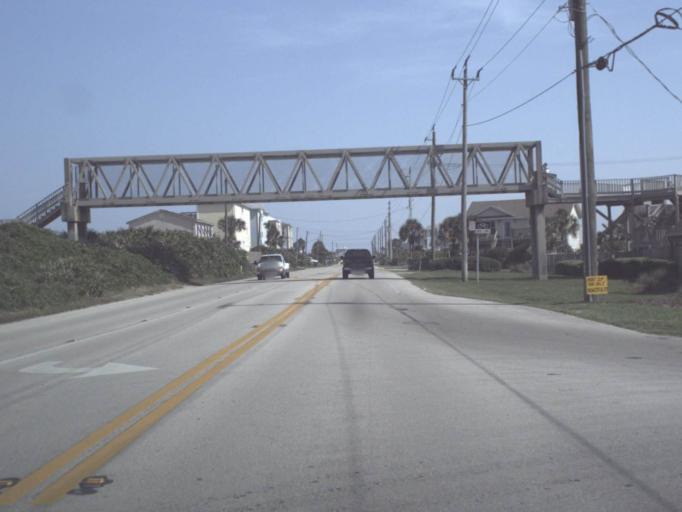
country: US
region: Florida
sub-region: Saint Johns County
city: Villano Beach
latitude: 29.9385
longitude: -81.2999
